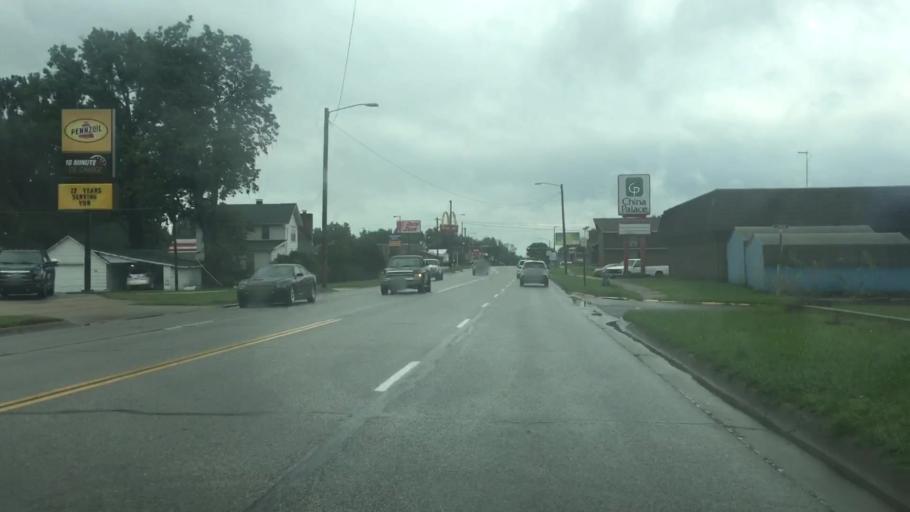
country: US
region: Kansas
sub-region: Allen County
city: Iola
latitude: 37.9240
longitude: -95.4091
